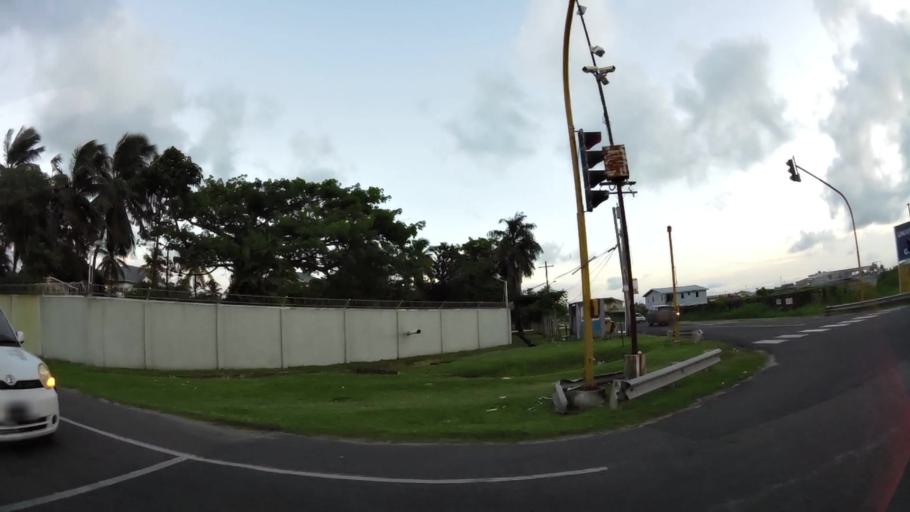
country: GY
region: Demerara-Mahaica
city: Georgetown
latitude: 6.8247
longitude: -58.1107
